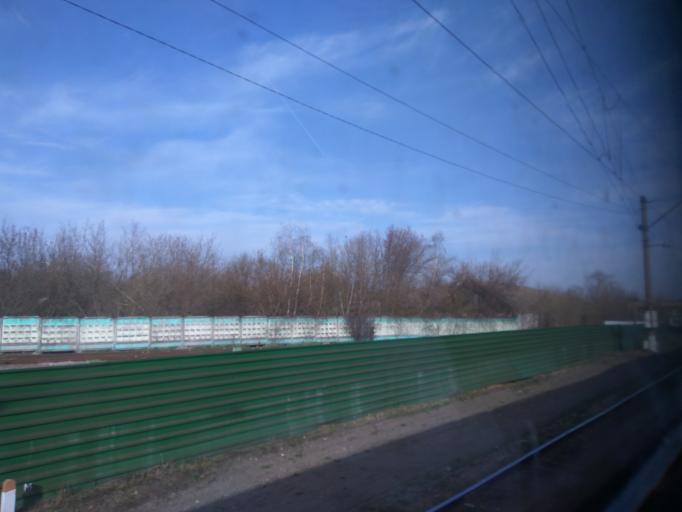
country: RU
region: Moskovskaya
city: Ramenskoye
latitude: 55.5573
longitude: 38.2487
